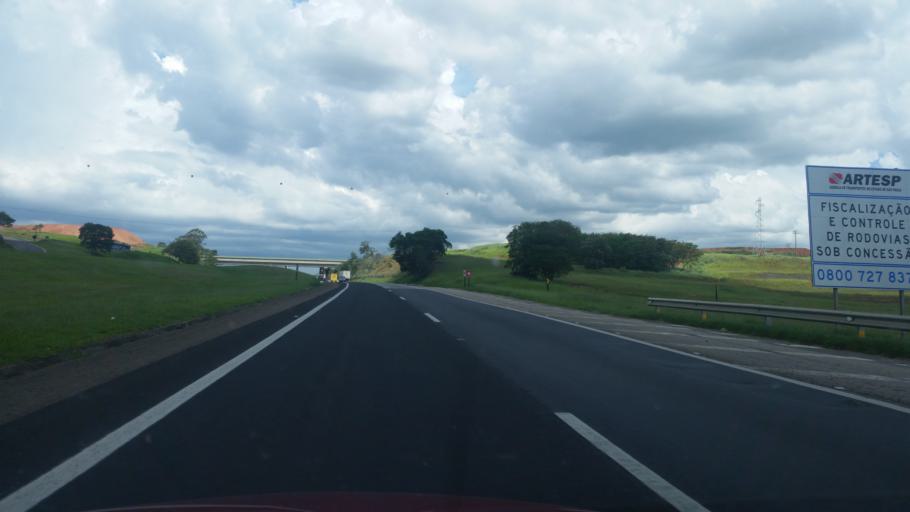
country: BR
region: Sao Paulo
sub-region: Tatui
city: Tatui
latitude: -23.2816
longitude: -47.8116
